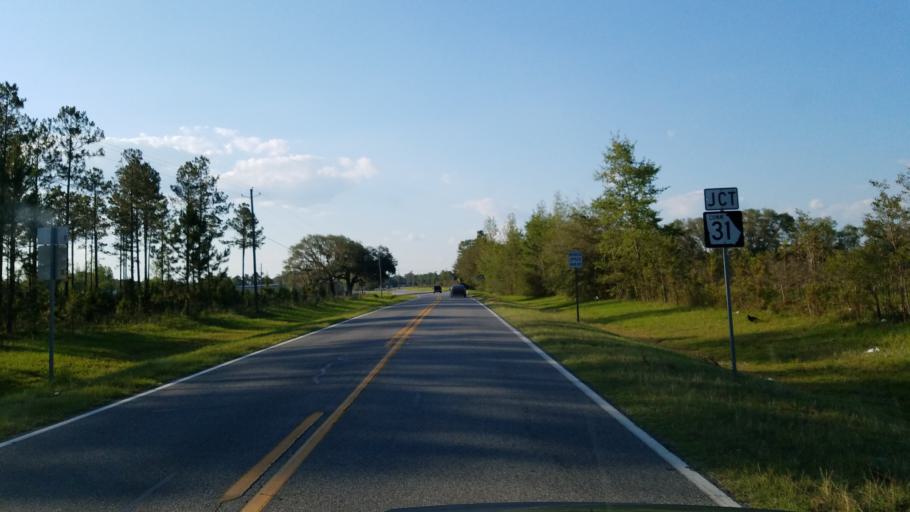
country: US
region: Georgia
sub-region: Lanier County
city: Lakeland
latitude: 31.0215
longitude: -83.0653
